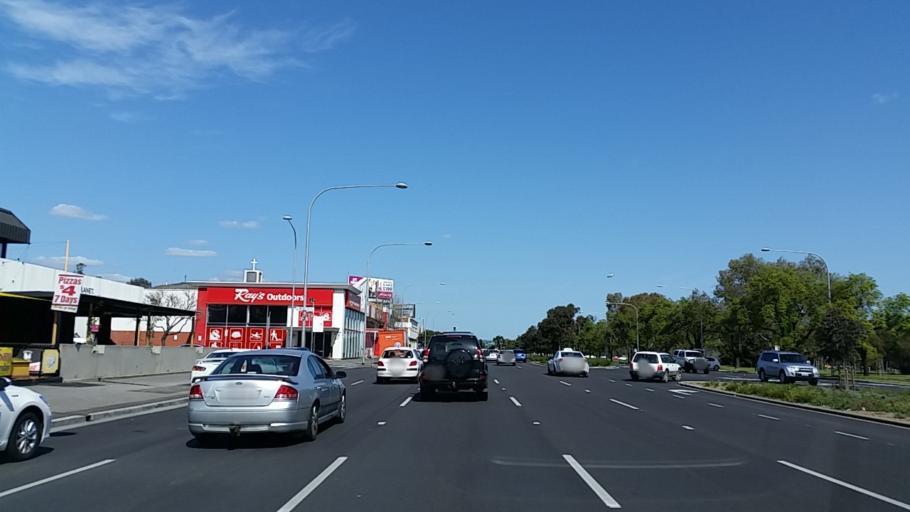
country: AU
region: South Australia
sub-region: Adelaide
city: Adelaide
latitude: -34.9259
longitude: 138.5877
